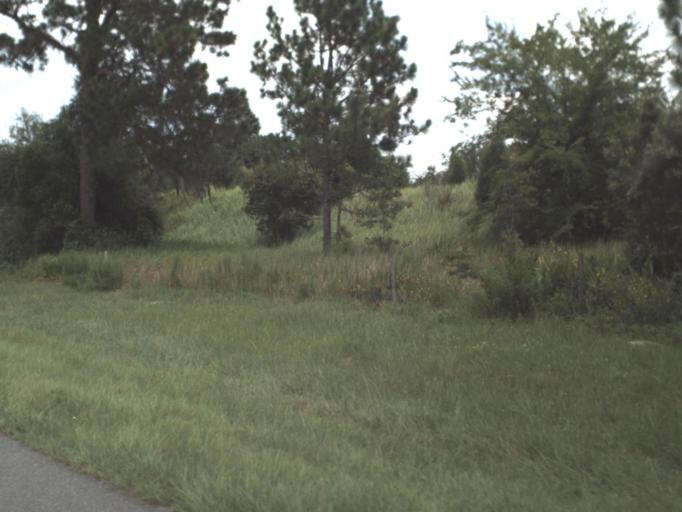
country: US
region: Florida
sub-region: Hernando County
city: Ridge Manor
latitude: 28.5133
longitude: -82.1690
